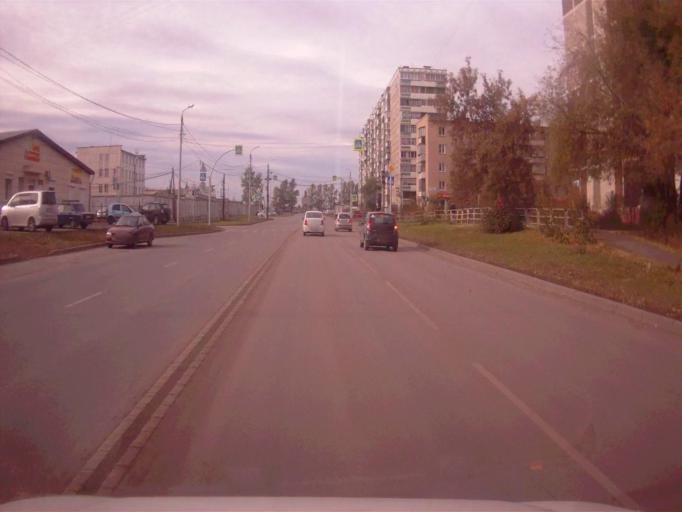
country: RU
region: Chelyabinsk
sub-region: Gorod Chelyabinsk
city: Chelyabinsk
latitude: 55.1169
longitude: 61.4238
